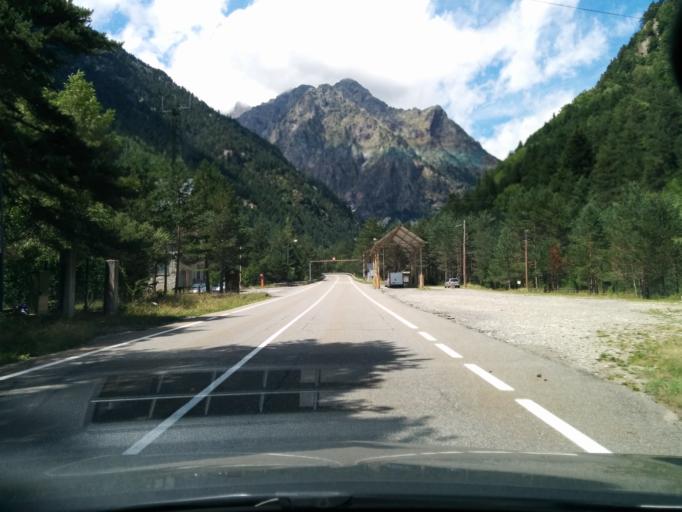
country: ES
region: Aragon
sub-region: Provincia de Huesca
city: Bielsa
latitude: 42.6884
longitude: 0.2084
